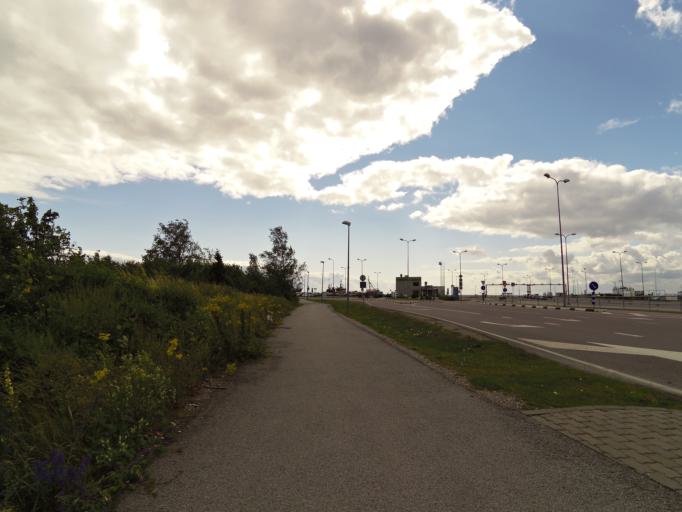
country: EE
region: Laeaene
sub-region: Haapsalu linn
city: Haapsalu
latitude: 58.9072
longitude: 23.4269
